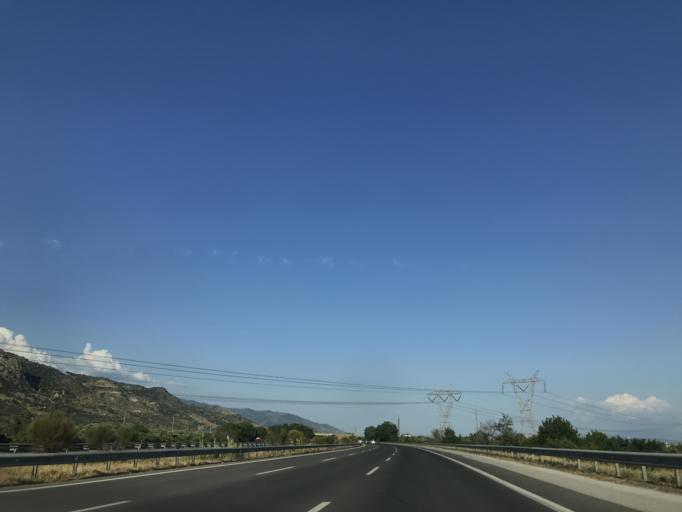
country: TR
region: Aydin
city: Incirliova
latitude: 37.8683
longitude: 27.7203
